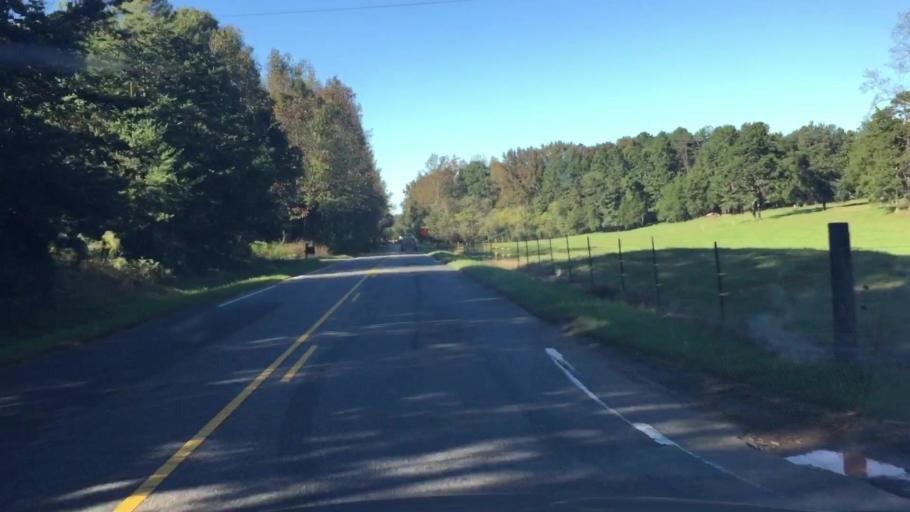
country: US
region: North Carolina
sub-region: Gaston County
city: Davidson
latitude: 35.5113
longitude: -80.7690
